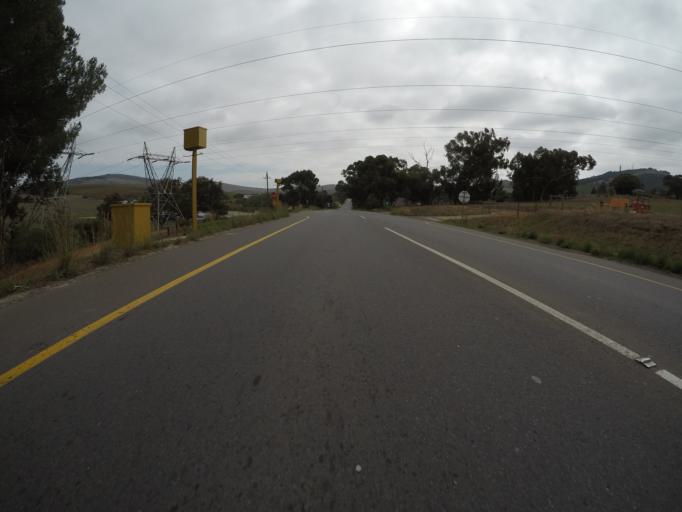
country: ZA
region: Western Cape
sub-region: City of Cape Town
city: Kraaifontein
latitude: -33.8417
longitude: 18.6145
